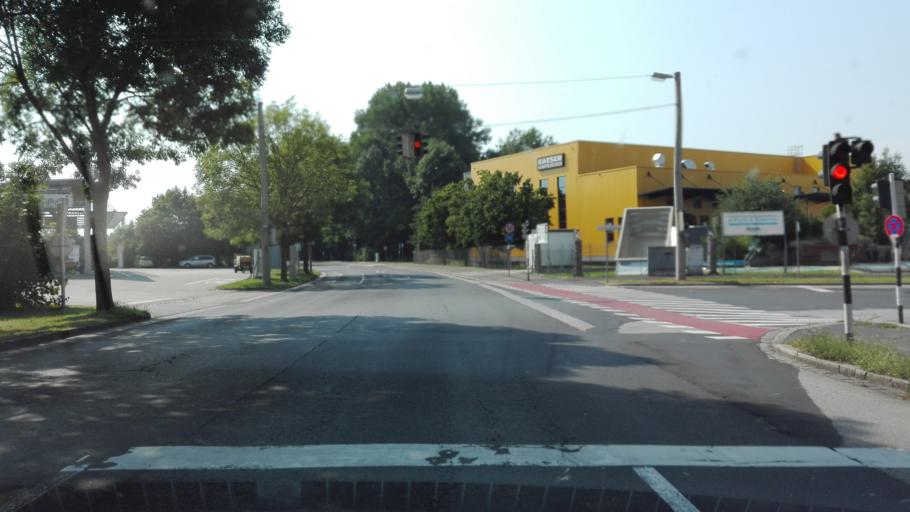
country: AT
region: Upper Austria
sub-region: Politischer Bezirk Linz-Land
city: Ansfelden
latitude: 48.2418
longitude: 14.2928
